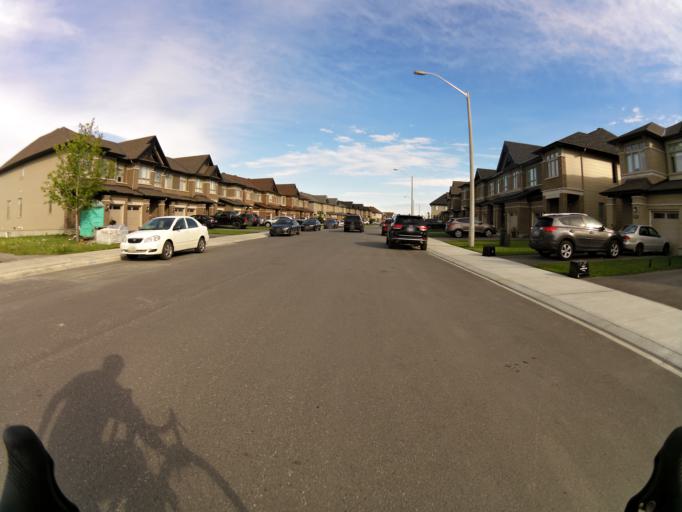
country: CA
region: Ontario
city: Bells Corners
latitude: 45.2709
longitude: -75.7802
